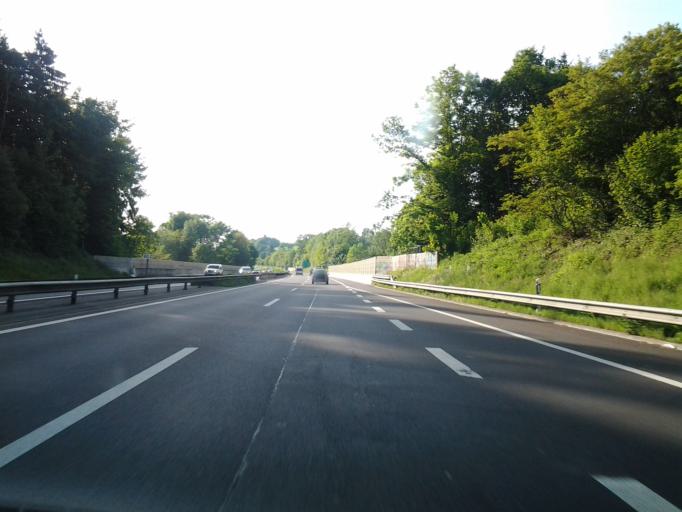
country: CH
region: Lucerne
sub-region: Sursee District
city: Sempach
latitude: 47.1388
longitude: 8.1958
